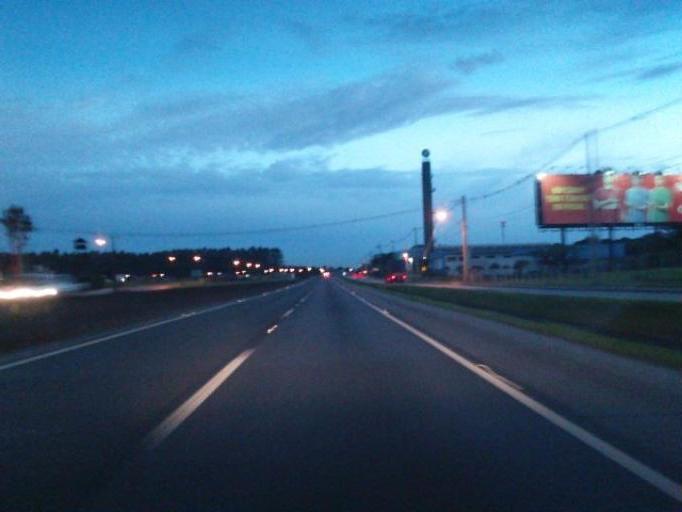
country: BR
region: Santa Catarina
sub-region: Barra Velha
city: Barra Velha
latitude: -26.5184
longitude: -48.7189
